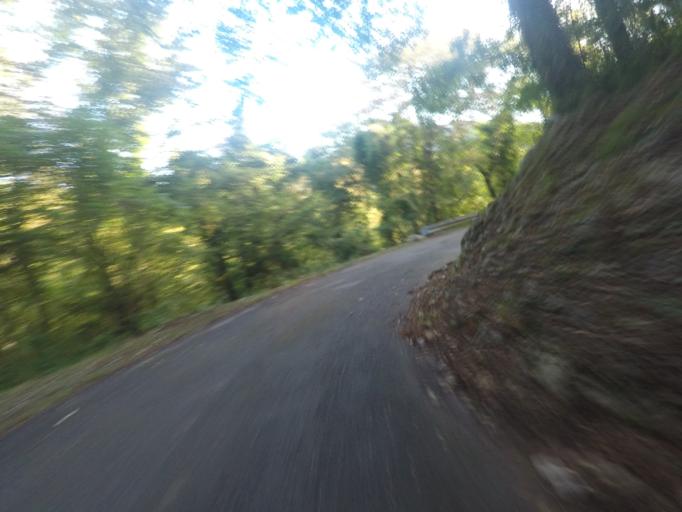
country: IT
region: Tuscany
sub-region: Provincia di Lucca
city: Pescaglia
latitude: 43.9389
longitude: 10.3846
